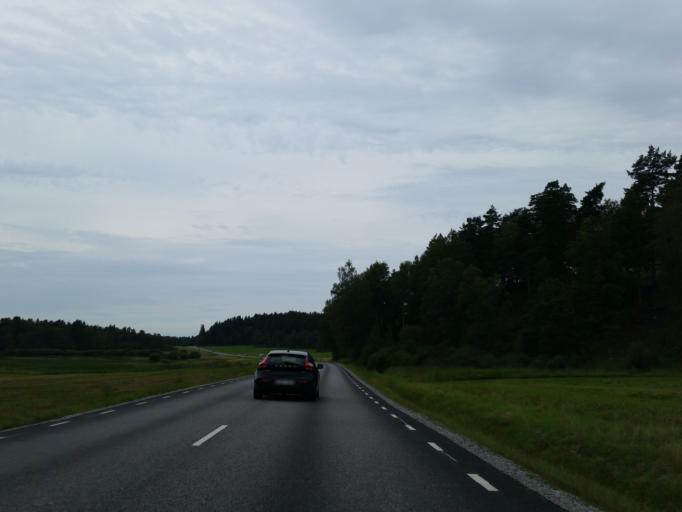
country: SE
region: Stockholm
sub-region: Salems Kommun
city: Ronninge
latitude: 59.2243
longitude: 17.7373
